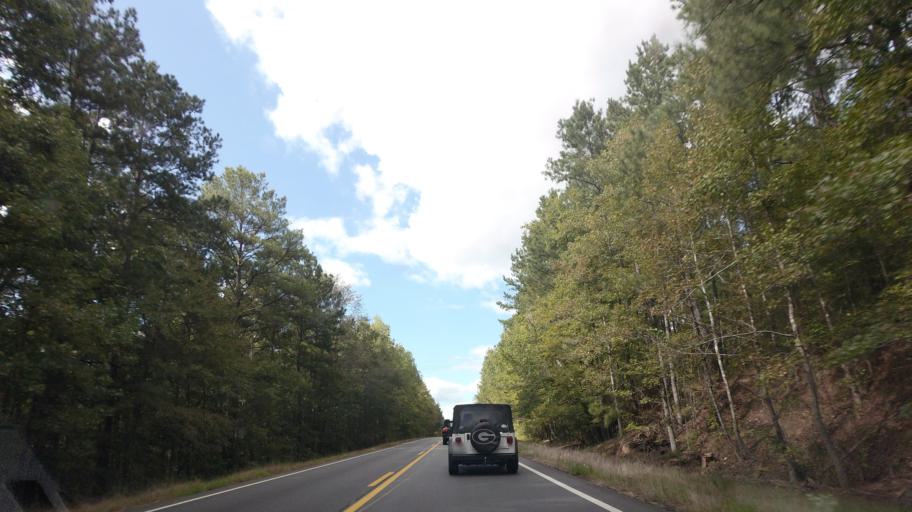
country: US
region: Georgia
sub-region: Monroe County
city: Forsyth
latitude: 33.0186
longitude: -83.7439
